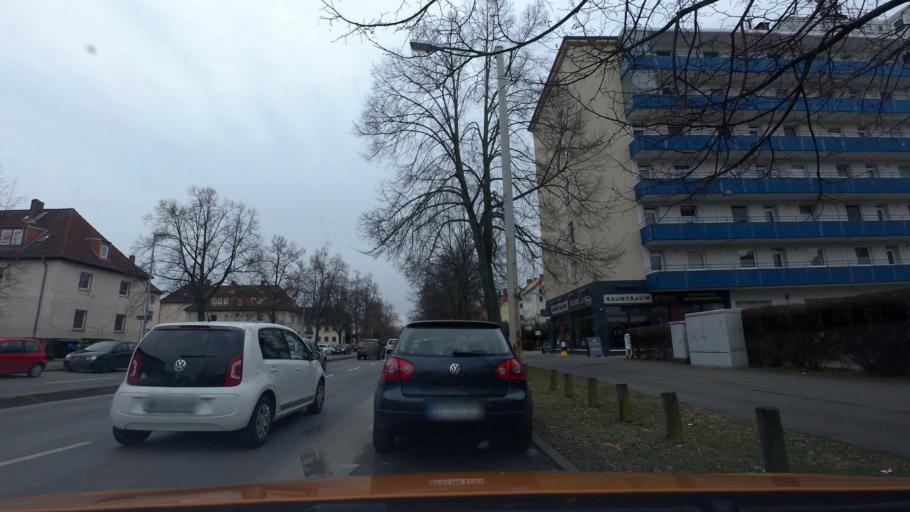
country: DE
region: Lower Saxony
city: Braunschweig
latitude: 52.2693
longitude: 10.5002
